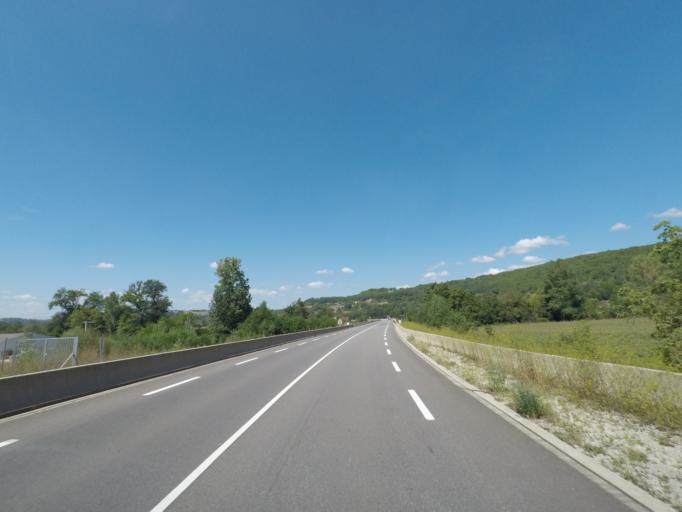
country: FR
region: Midi-Pyrenees
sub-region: Departement du Lot
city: Figeac
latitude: 44.5890
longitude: 1.9966
